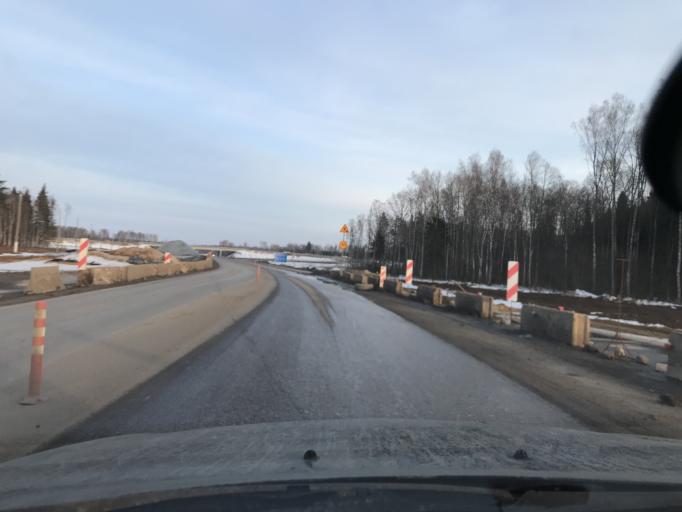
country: RU
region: Kaluga
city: Kaluga
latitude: 54.4619
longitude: 36.2659
